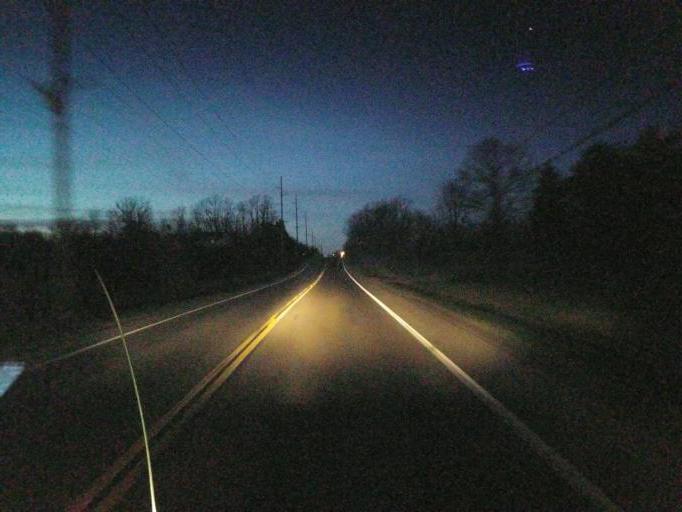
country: US
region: Ohio
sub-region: Logan County
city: Bellefontaine
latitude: 40.3916
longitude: -83.7509
